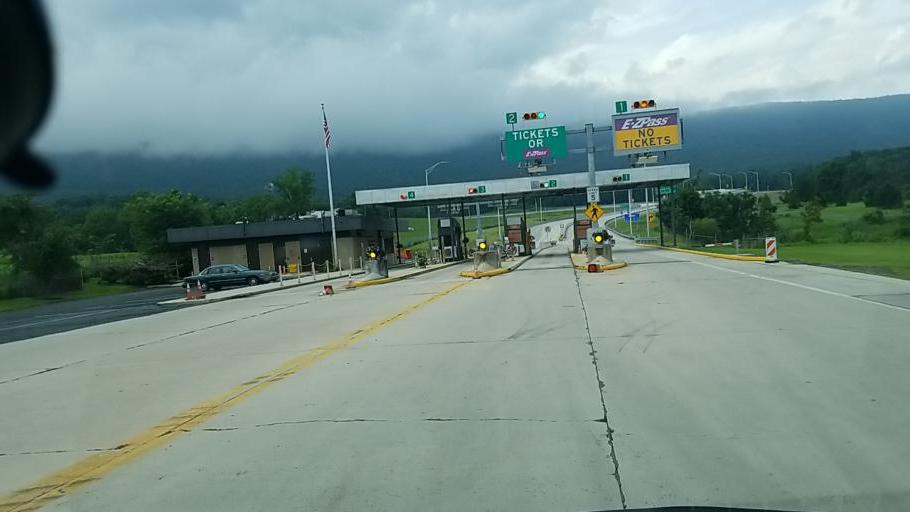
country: US
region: Pennsylvania
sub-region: Franklin County
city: Doylestown
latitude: 40.1531
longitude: -77.6126
